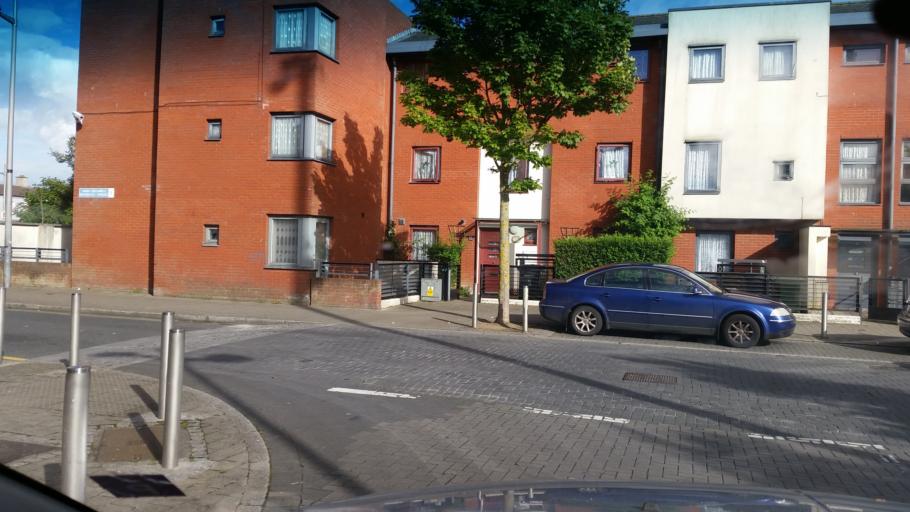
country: IE
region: Leinster
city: Ballymun
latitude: 53.3981
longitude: -6.2571
